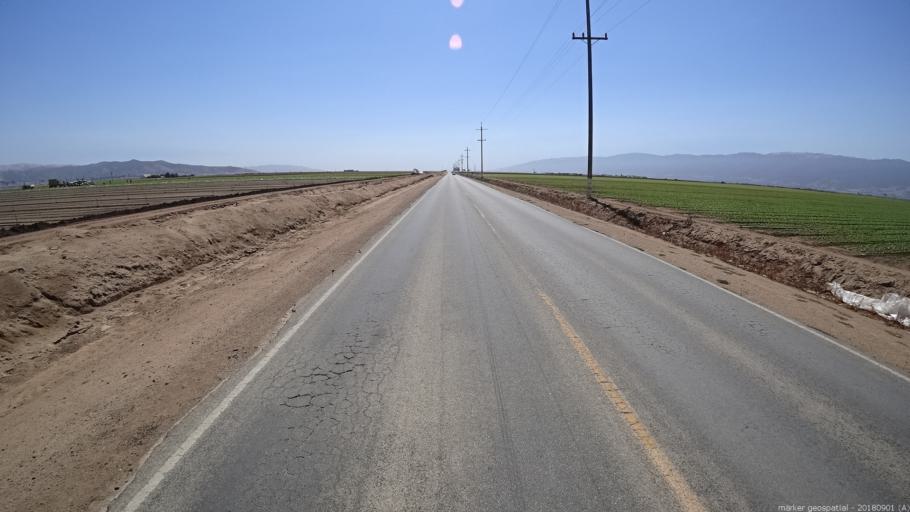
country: US
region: California
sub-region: Monterey County
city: Chualar
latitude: 36.5974
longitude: -121.5079
